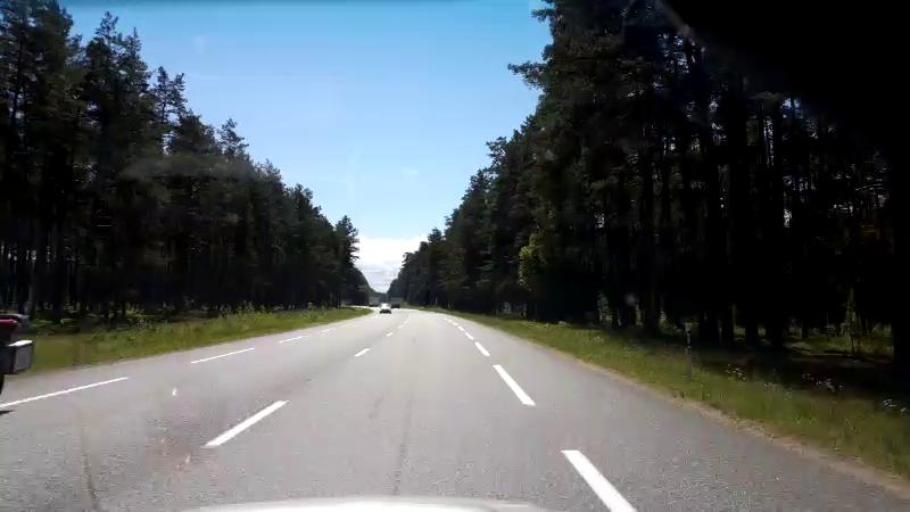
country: LV
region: Saulkrastu
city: Saulkrasti
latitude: 57.3478
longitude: 24.4397
